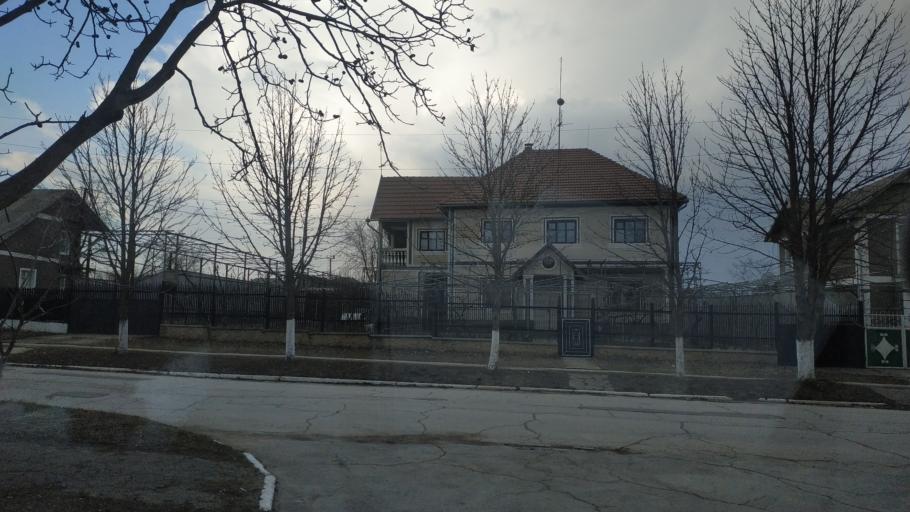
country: MD
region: Telenesti
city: Grigoriopol
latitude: 47.0124
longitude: 29.2908
